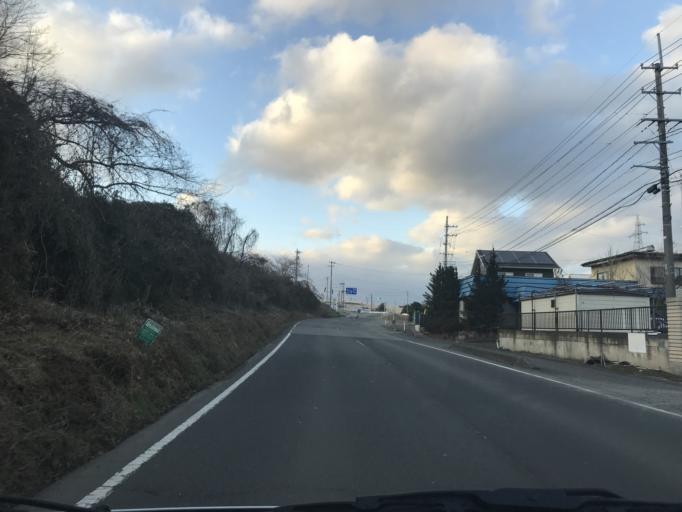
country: JP
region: Miyagi
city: Furukawa
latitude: 38.6680
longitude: 141.0101
